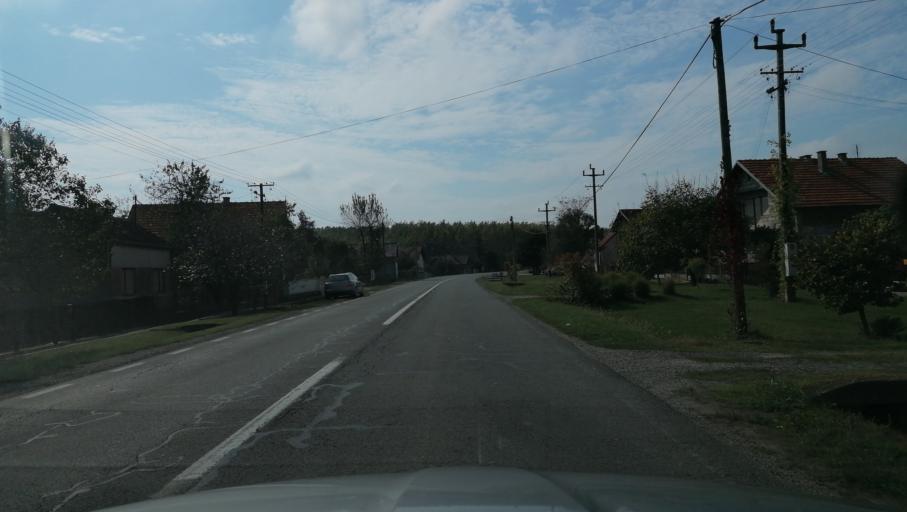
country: RS
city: Bosut
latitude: 44.9255
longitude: 19.3551
